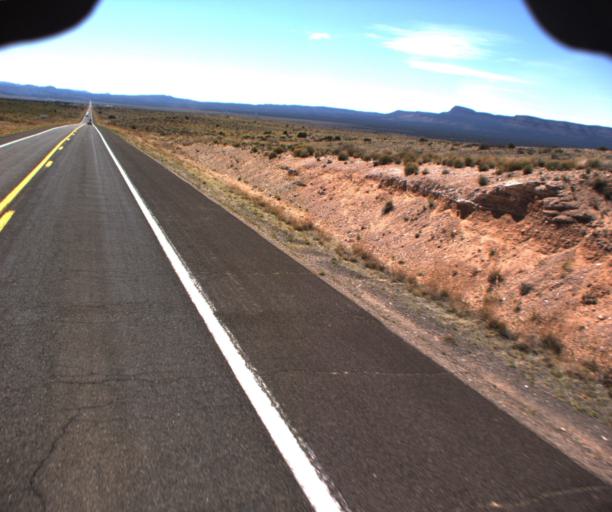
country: US
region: Arizona
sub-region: Mohave County
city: Peach Springs
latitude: 35.5167
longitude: -113.4974
